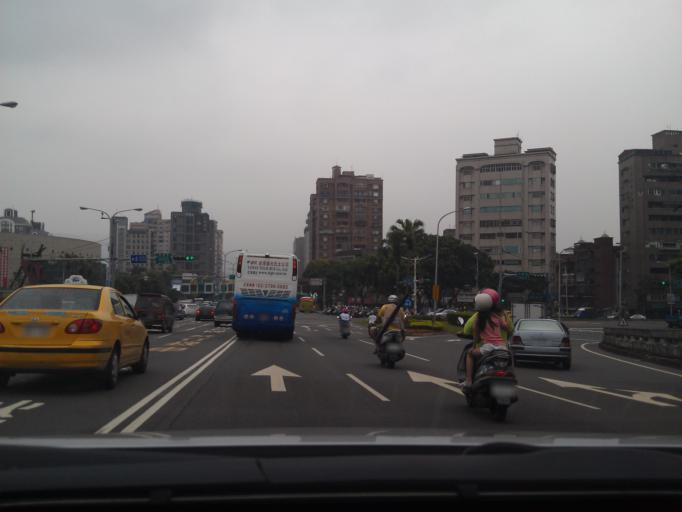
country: TW
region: Taipei
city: Taipei
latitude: 25.0905
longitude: 121.5158
